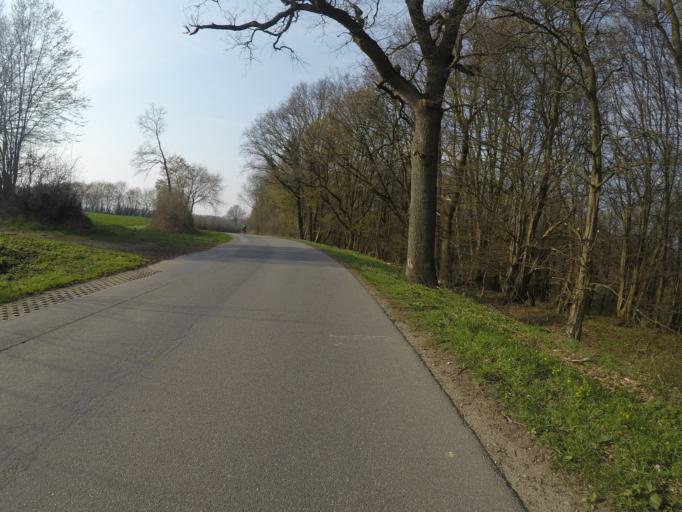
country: DE
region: Schleswig-Holstein
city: Kukels
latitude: 53.8859
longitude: 10.2424
